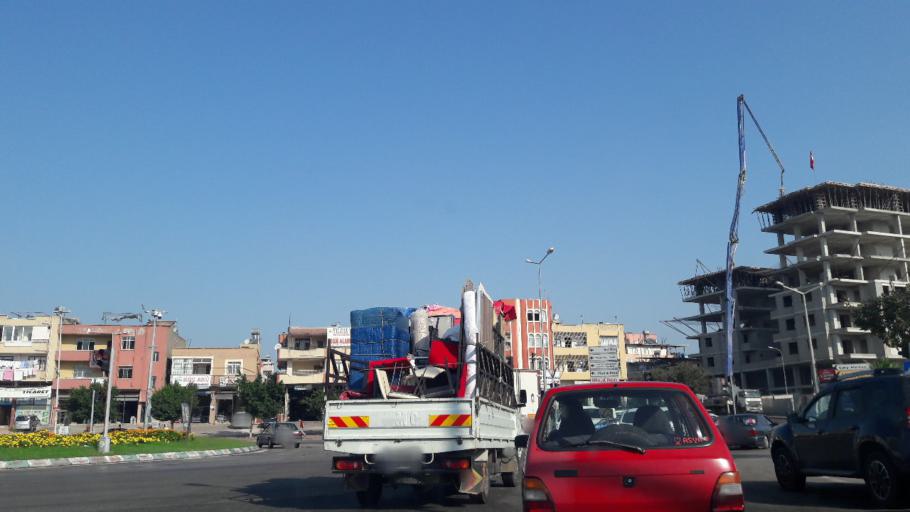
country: TR
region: Adana
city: Yuregir
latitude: 37.0249
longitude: 35.3996
